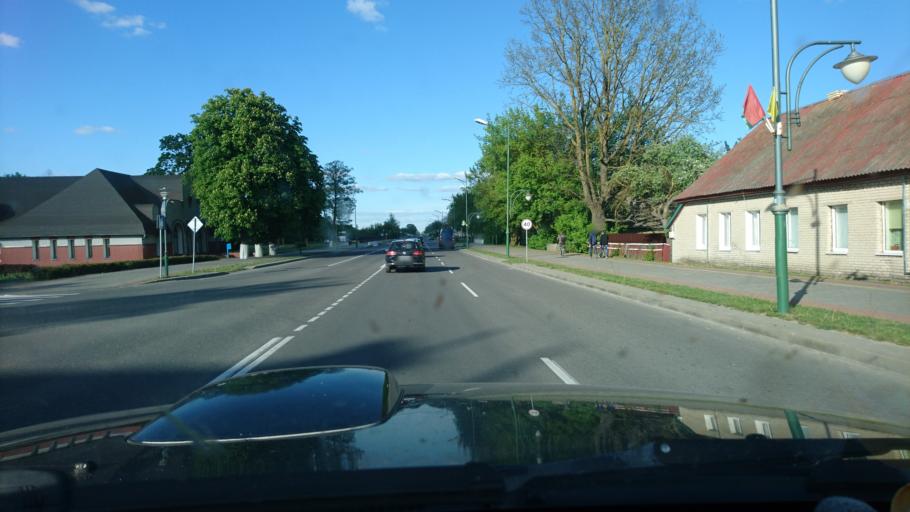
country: BY
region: Brest
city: Byaroza
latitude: 52.5356
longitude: 24.9873
